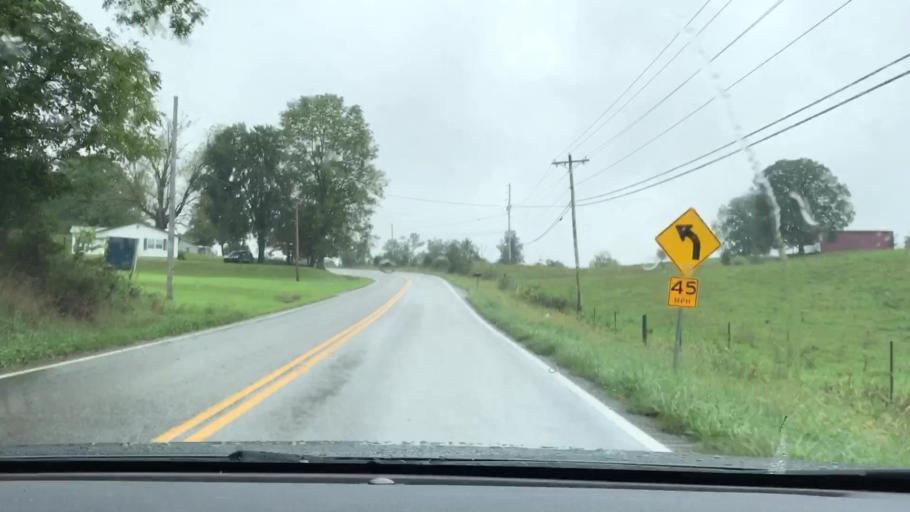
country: US
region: Kentucky
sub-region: Monroe County
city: Tompkinsville
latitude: 36.6901
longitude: -85.7140
